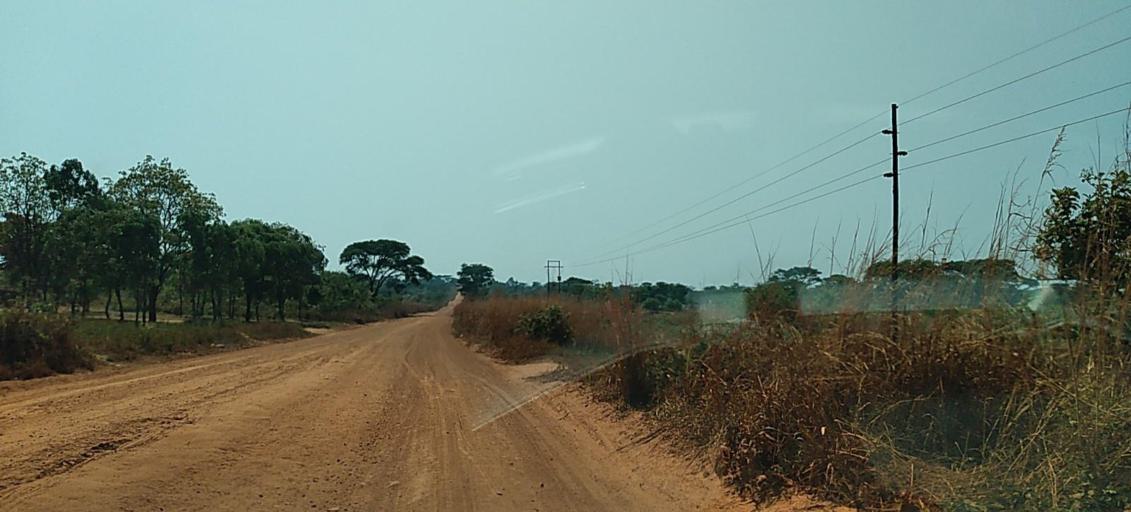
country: ZM
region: North-Western
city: Kansanshi
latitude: -12.0052
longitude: 26.5662
